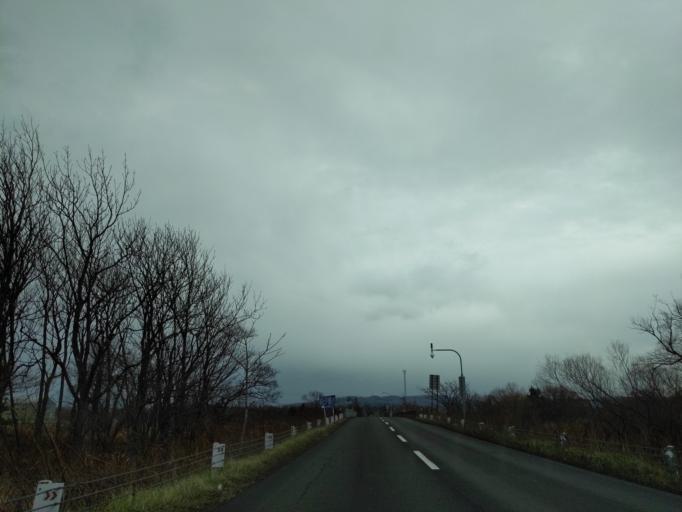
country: JP
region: Hokkaido
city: Kitahiroshima
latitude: 43.0446
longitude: 141.6752
